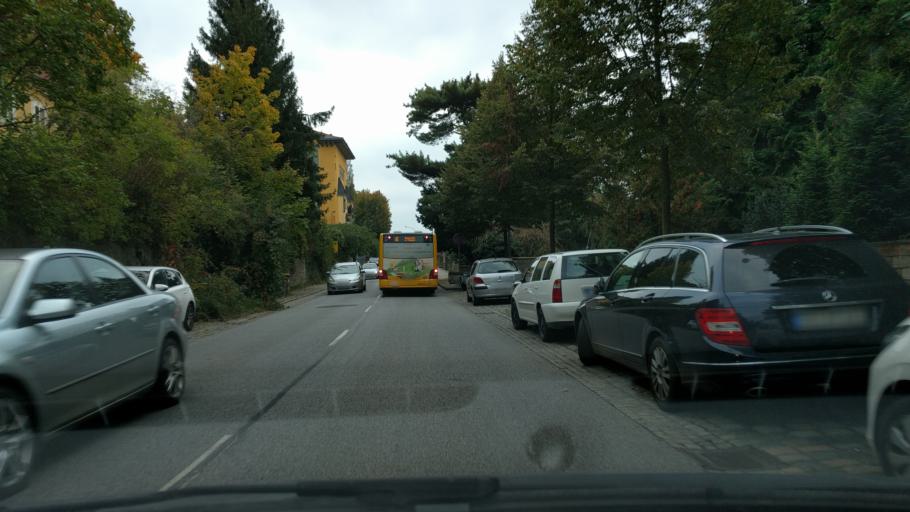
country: DE
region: Saxony
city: Albertstadt
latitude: 51.0469
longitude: 13.8221
